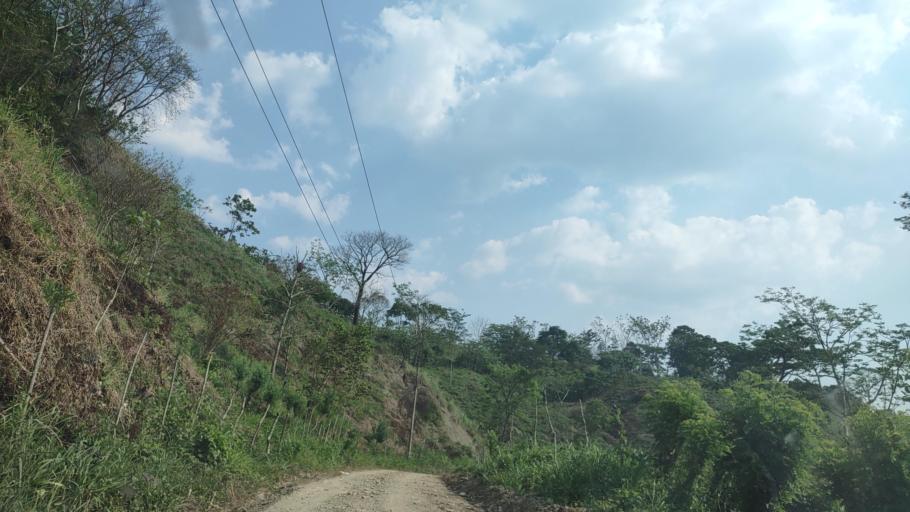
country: MX
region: Chiapas
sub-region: Tecpatan
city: Raudales Malpaso
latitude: 17.3186
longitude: -93.7410
